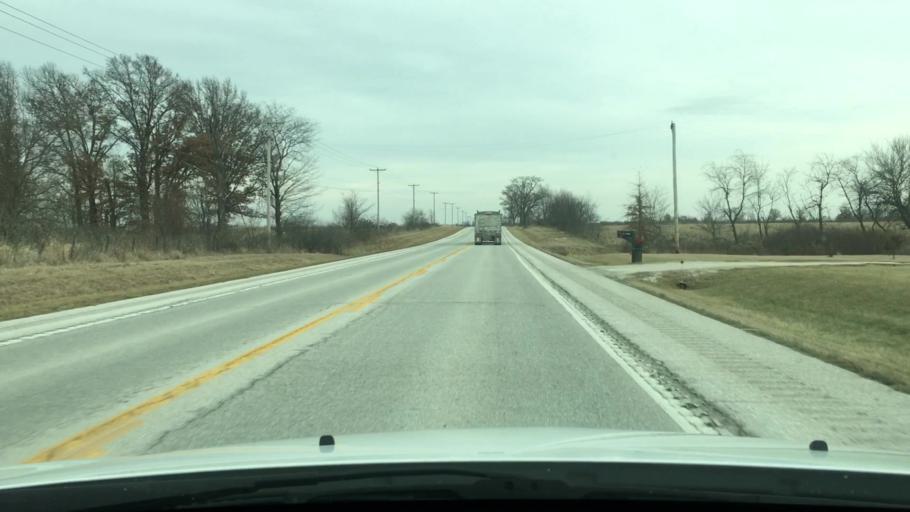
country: US
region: Missouri
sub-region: Pike County
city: Bowling Green
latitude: 39.3443
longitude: -91.2663
